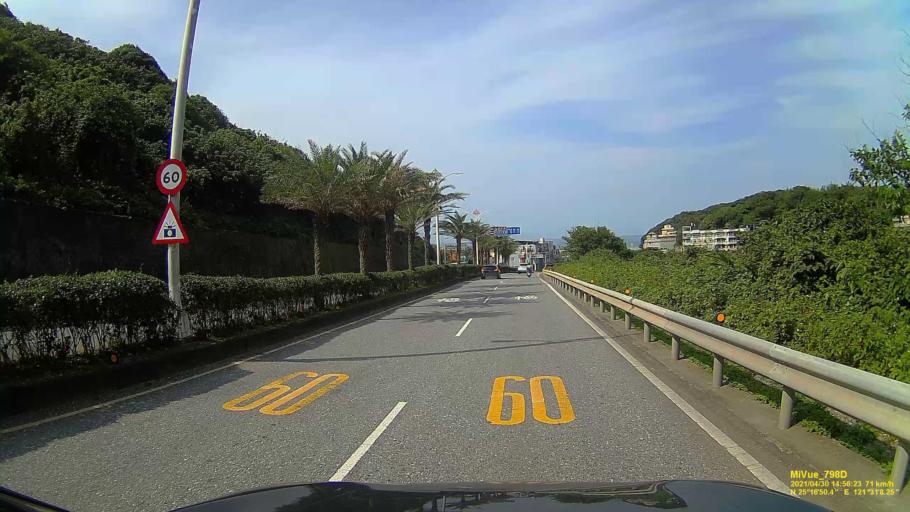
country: TW
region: Taipei
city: Taipei
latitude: 25.2811
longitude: 121.5191
